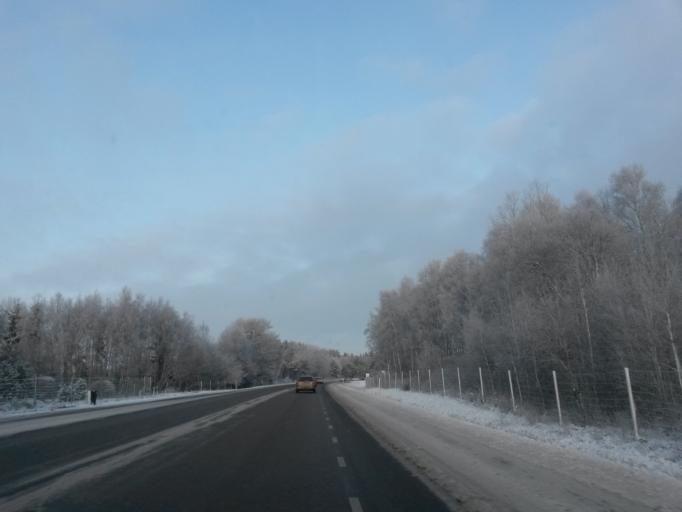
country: SE
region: Vaestra Goetaland
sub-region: Vara Kommun
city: Vara
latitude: 58.2059
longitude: 12.9000
